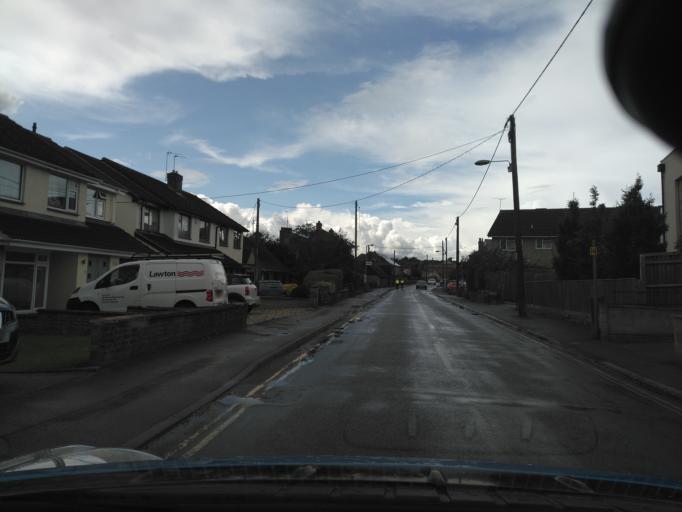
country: GB
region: England
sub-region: Oxfordshire
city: Wheatley
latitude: 51.7470
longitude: -1.1316
